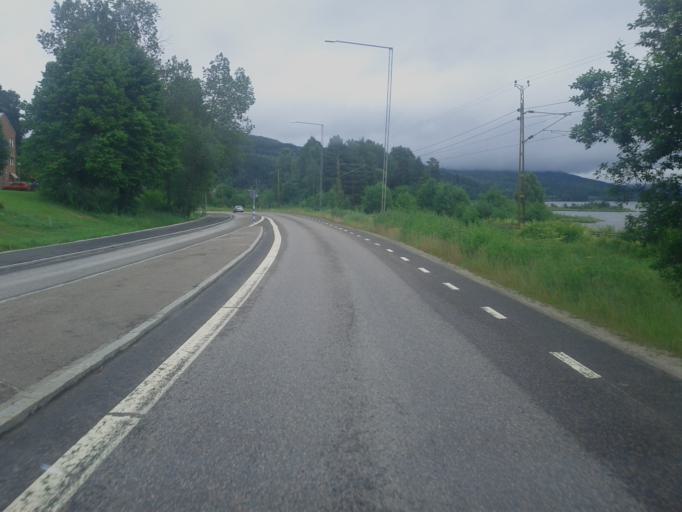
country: SE
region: Vaesternorrland
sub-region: Ange Kommun
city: Fransta
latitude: 62.4178
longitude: 16.5866
